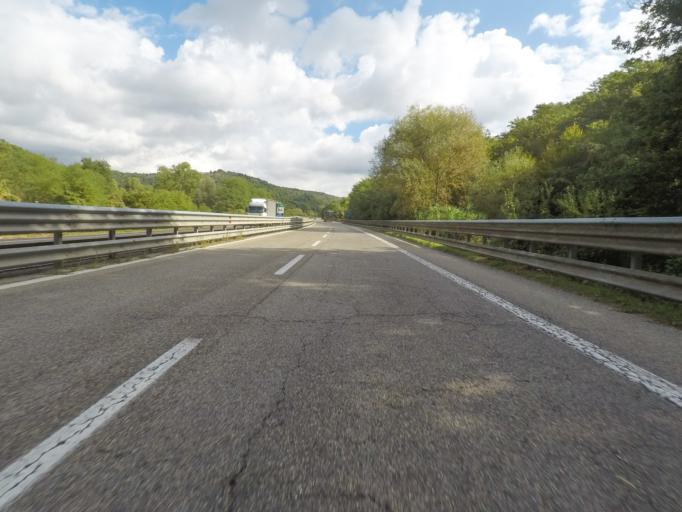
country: IT
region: Tuscany
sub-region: Province of Arezzo
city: Lucignano
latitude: 43.2539
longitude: 11.6854
